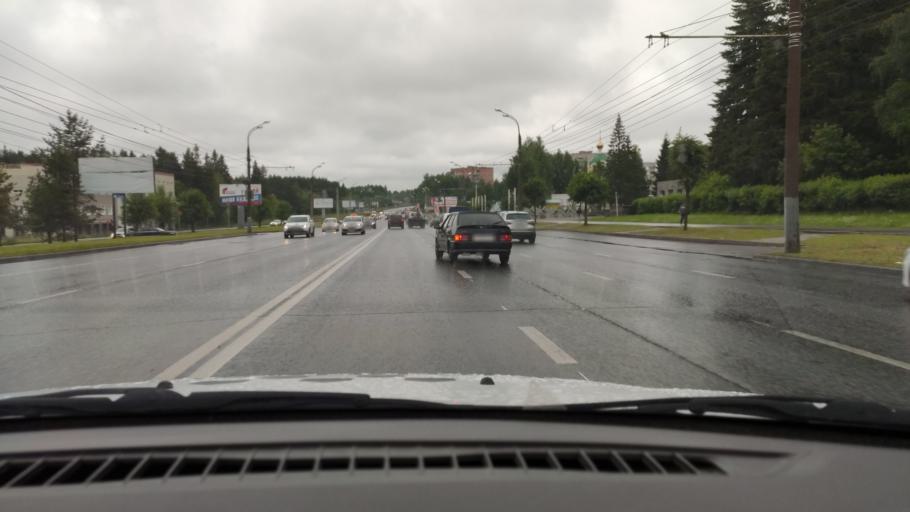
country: RU
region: Udmurtiya
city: Izhevsk
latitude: 56.8803
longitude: 53.2237
